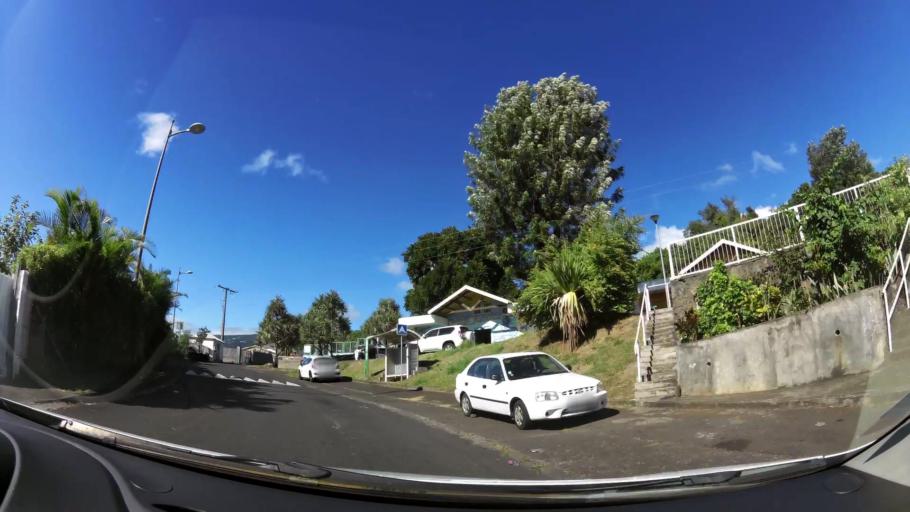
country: RE
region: Reunion
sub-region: Reunion
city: Saint-Denis
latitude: -20.9157
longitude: 55.4864
